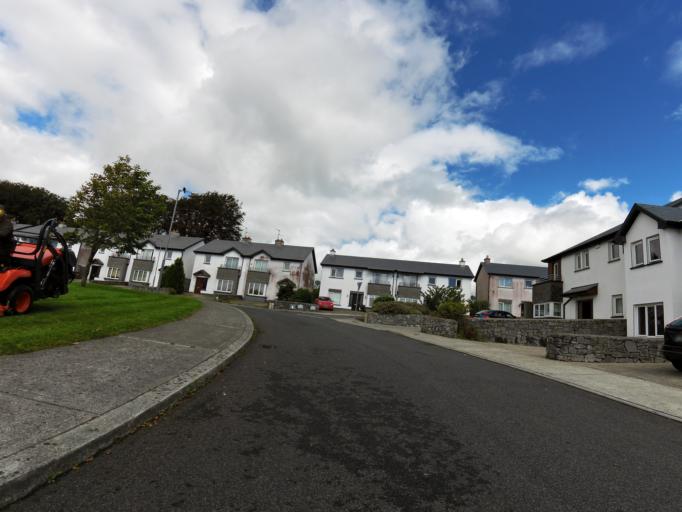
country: IE
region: Connaught
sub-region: County Galway
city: Loughrea
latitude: 53.1964
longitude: -8.5553
